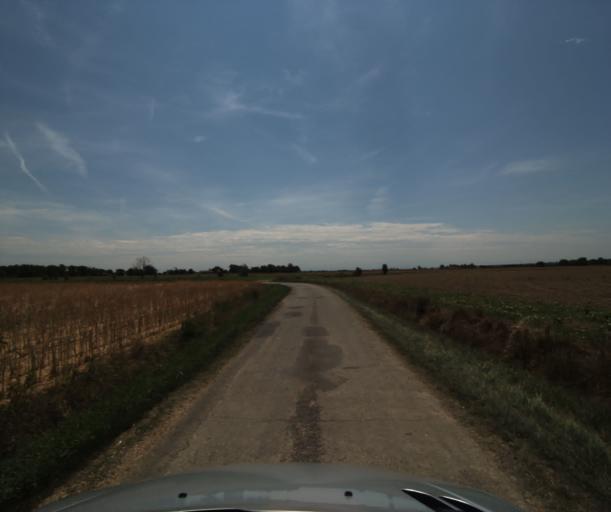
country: FR
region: Midi-Pyrenees
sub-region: Departement de la Haute-Garonne
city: Labastidette
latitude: 43.4622
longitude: 1.2597
